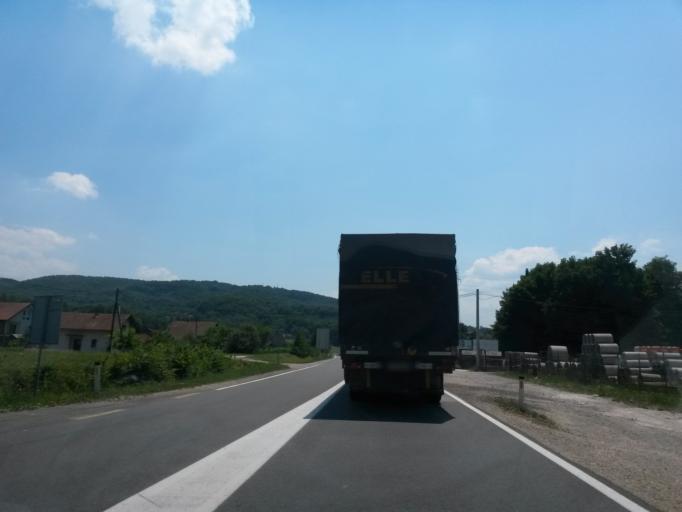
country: BA
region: Federation of Bosnia and Herzegovina
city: Lijesnica
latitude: 44.4775
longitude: 18.0680
